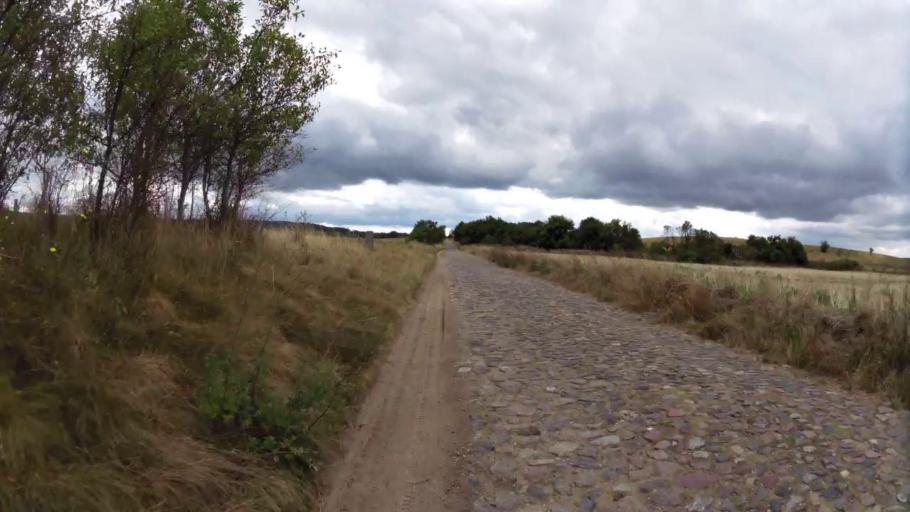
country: PL
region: West Pomeranian Voivodeship
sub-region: Powiat mysliborski
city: Debno
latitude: 52.8348
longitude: 14.7175
